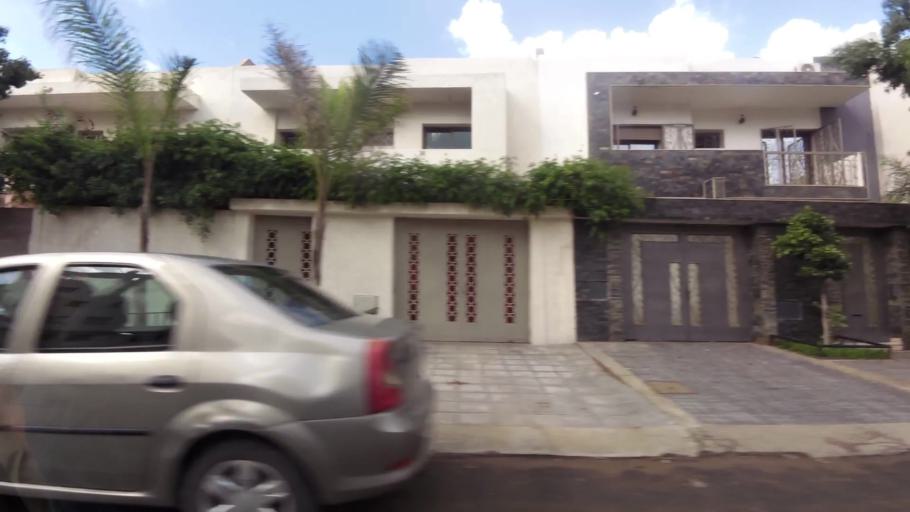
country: MA
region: Grand Casablanca
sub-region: Casablanca
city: Casablanca
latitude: 33.5393
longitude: -7.6866
